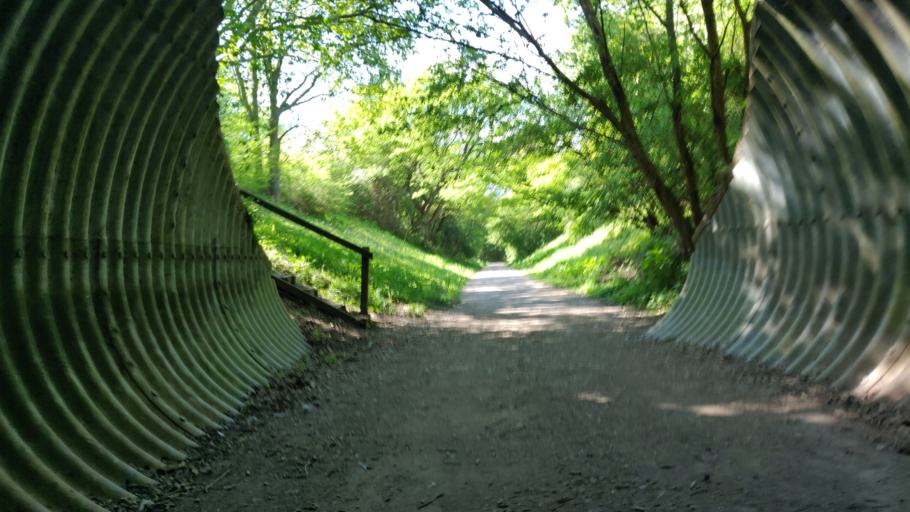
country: GB
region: England
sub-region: West Sussex
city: Rudgwick
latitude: 51.0691
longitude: -0.4175
